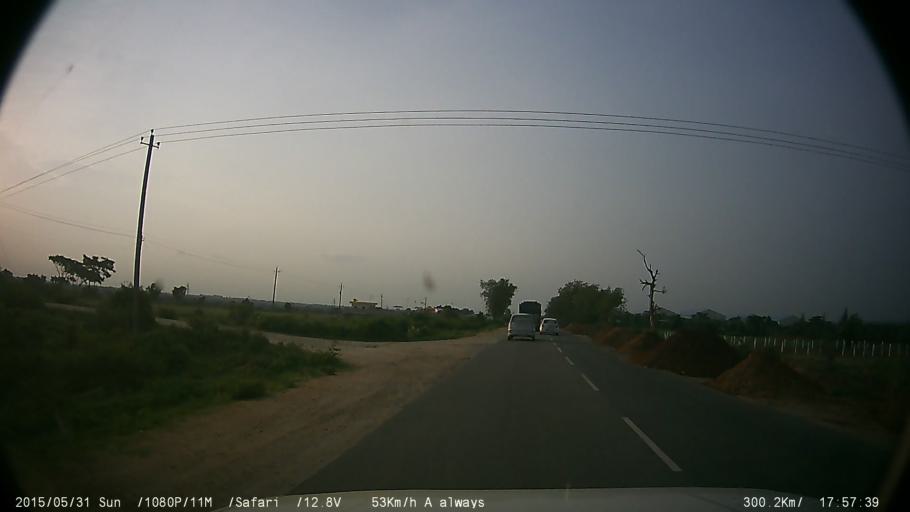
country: IN
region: Karnataka
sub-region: Mysore
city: Nanjangud
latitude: 12.0029
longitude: 76.6691
